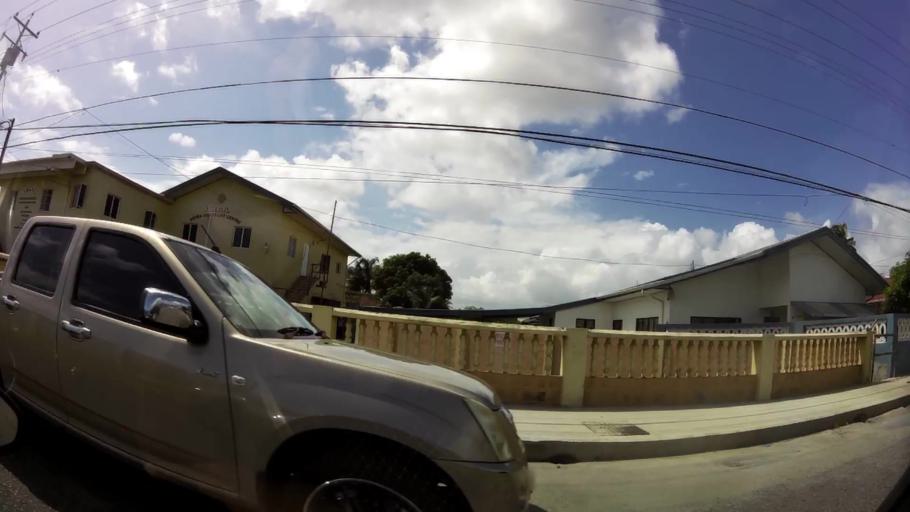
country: TT
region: Borough of Arima
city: Arima
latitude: 10.6281
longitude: -61.2815
